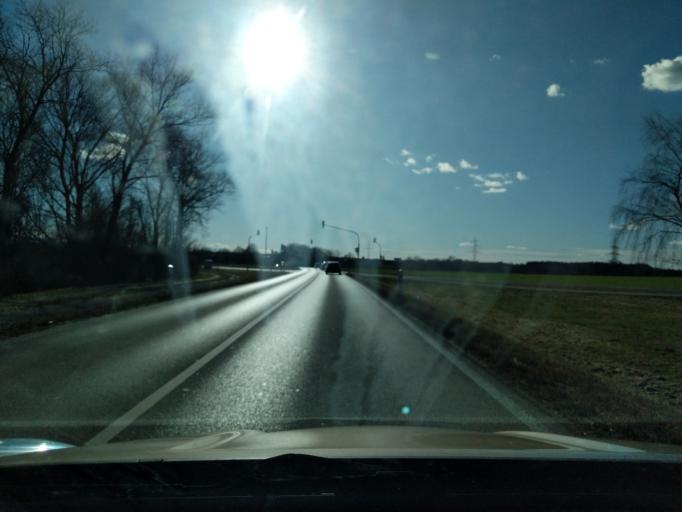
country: DE
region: Bavaria
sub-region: Upper Bavaria
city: Zorneding
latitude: 48.0987
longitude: 11.8270
